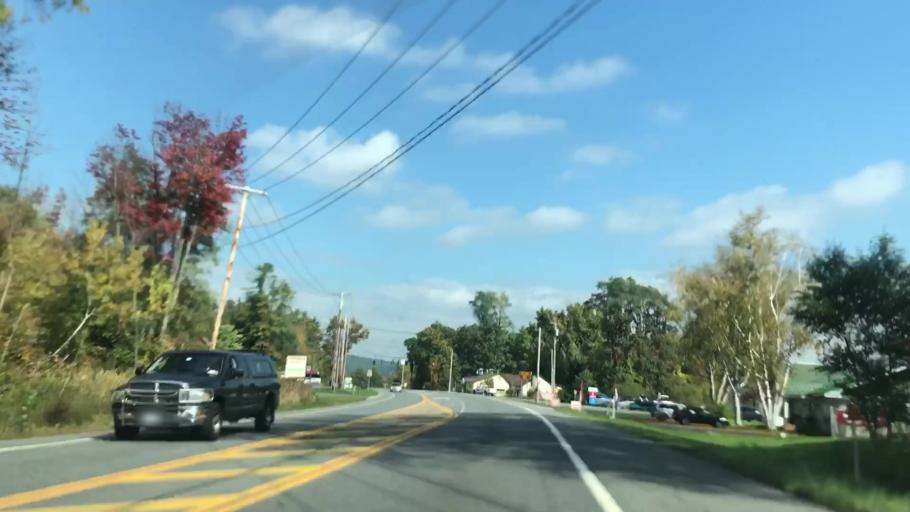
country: US
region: New York
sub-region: Warren County
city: Queensbury
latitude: 43.3873
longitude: -73.6477
